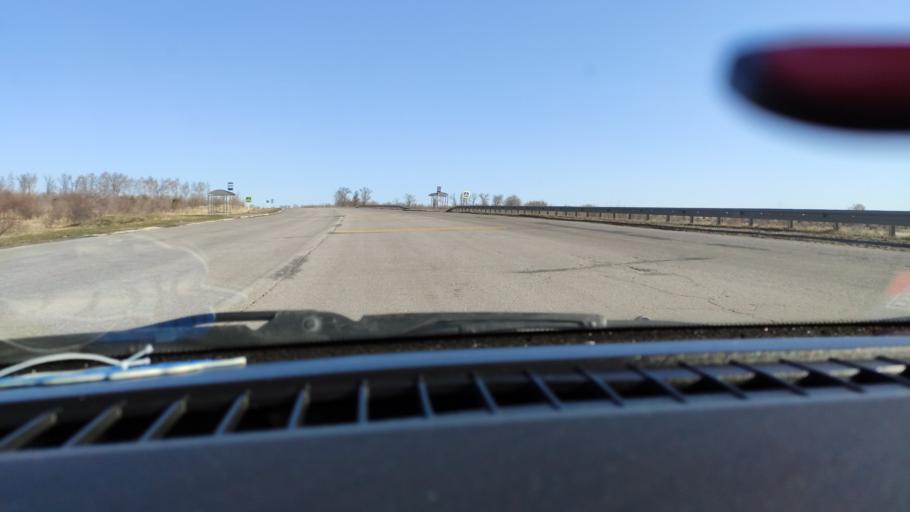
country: RU
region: Samara
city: Varlamovo
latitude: 53.1043
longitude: 48.3570
